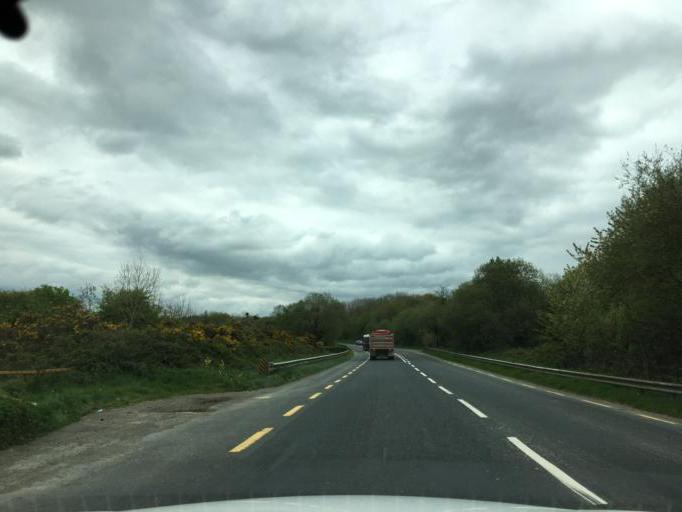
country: IE
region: Leinster
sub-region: Loch Garman
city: New Ross
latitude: 52.4197
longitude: -6.9294
